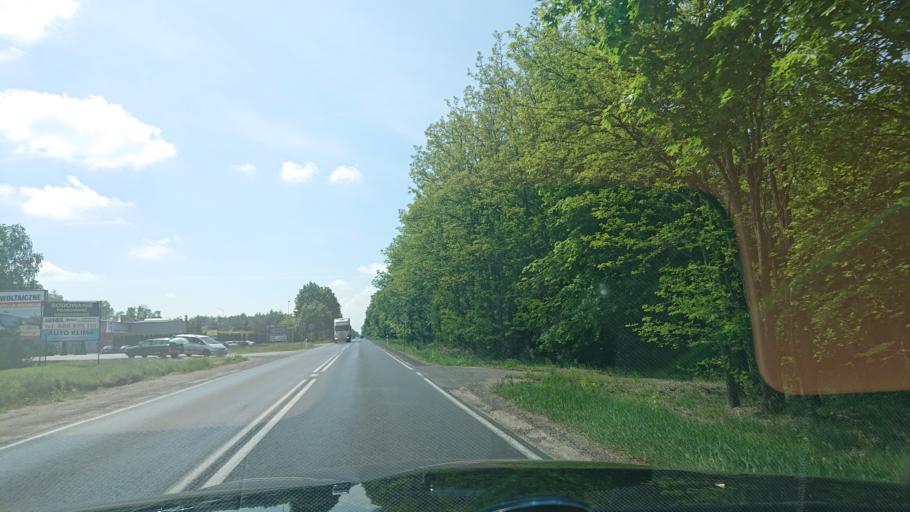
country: PL
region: Greater Poland Voivodeship
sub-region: Powiat gnieznienski
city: Gniezno
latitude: 52.4811
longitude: 17.5932
